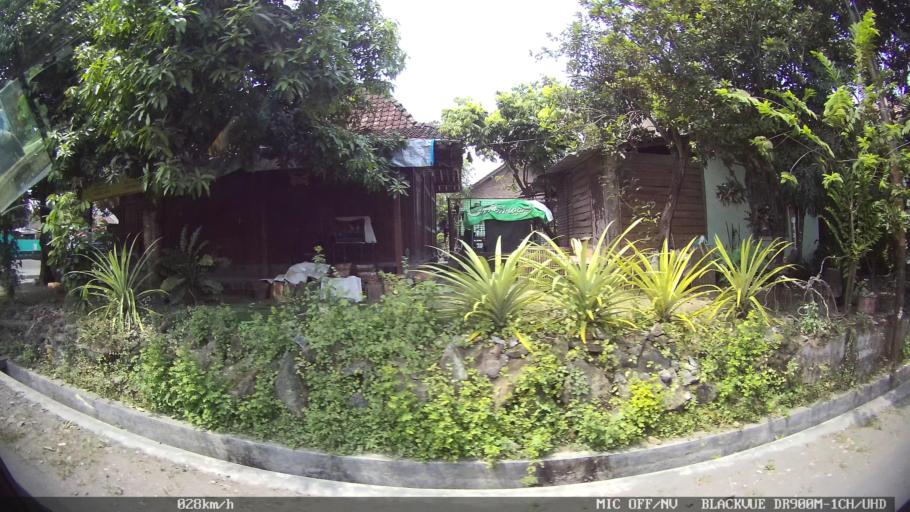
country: ID
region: Daerah Istimewa Yogyakarta
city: Yogyakarta
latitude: -7.8185
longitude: 110.4077
